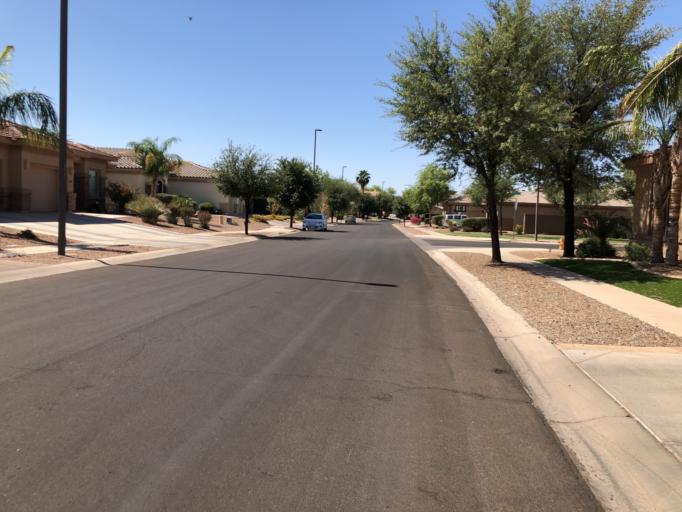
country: US
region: Arizona
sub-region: Maricopa County
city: Queen Creek
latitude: 33.2686
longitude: -111.6888
